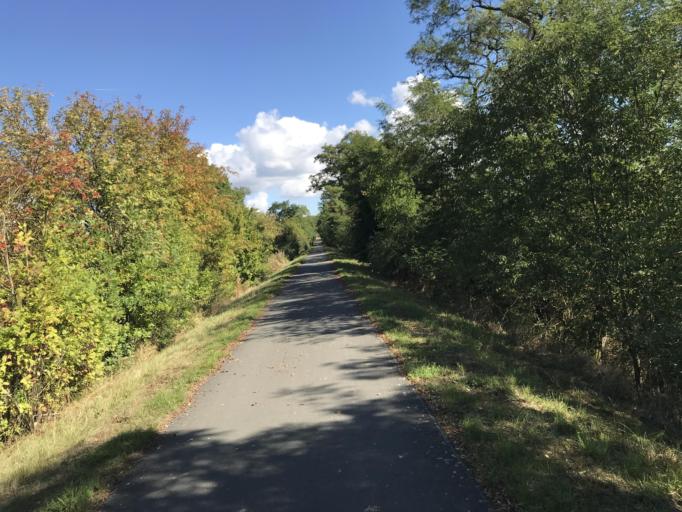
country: DE
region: Hesse
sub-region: Regierungsbezirk Kassel
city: Sachsenhausen
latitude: 51.2646
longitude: 8.9619
